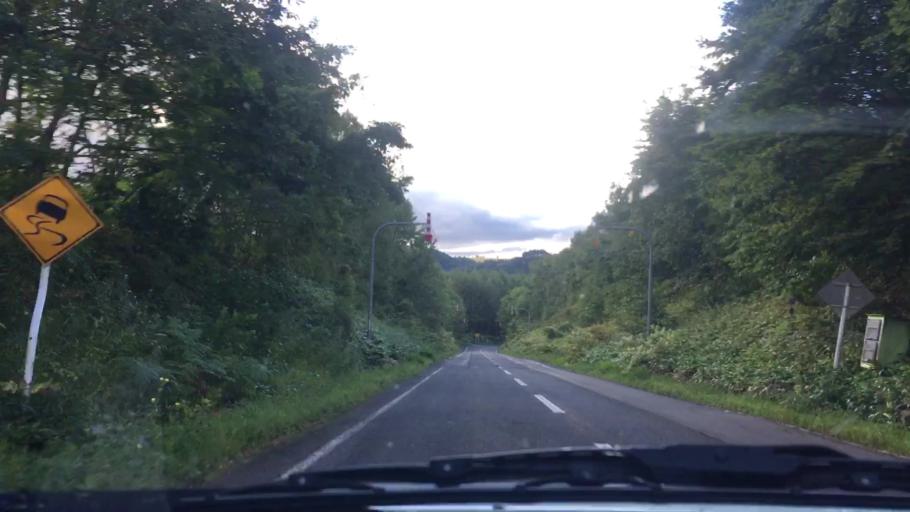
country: JP
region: Hokkaido
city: Otofuke
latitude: 43.1753
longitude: 142.9281
